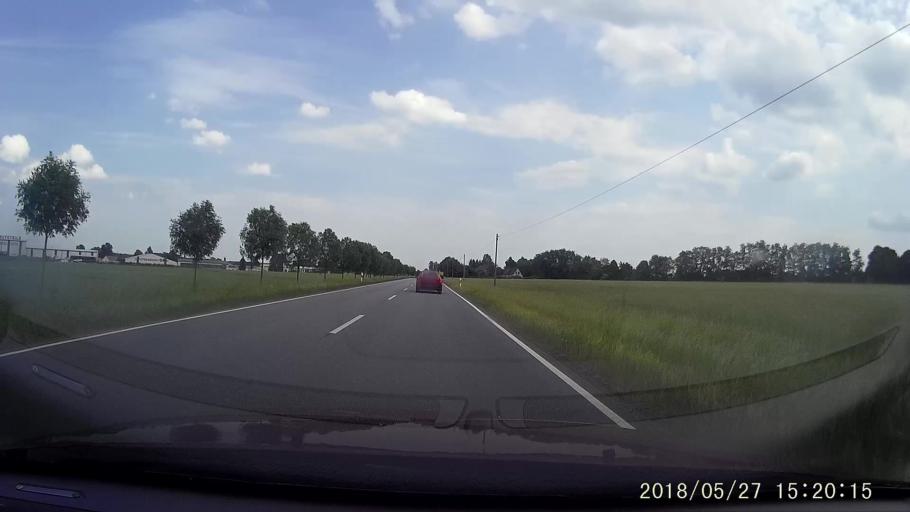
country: DE
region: Saxony
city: Kodersdorf
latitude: 51.2487
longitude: 14.8843
